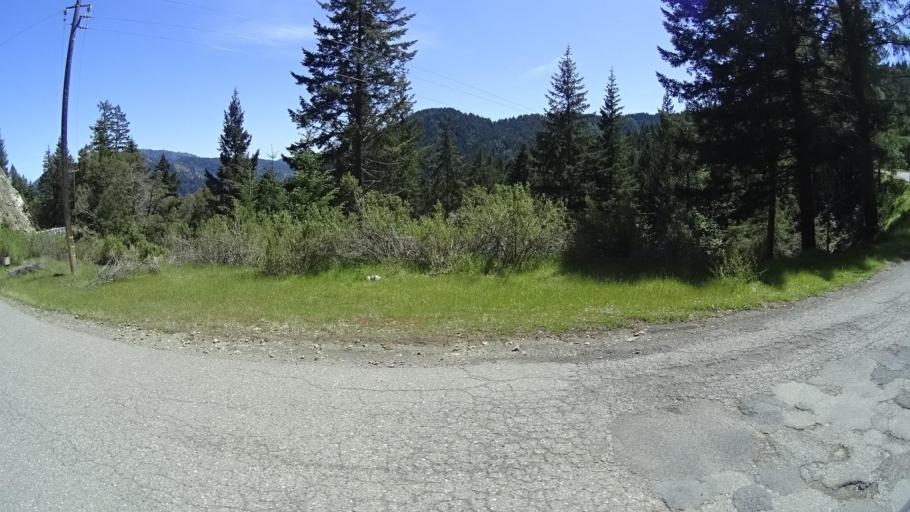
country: US
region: California
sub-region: Humboldt County
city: Rio Dell
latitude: 40.3216
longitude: -124.0593
